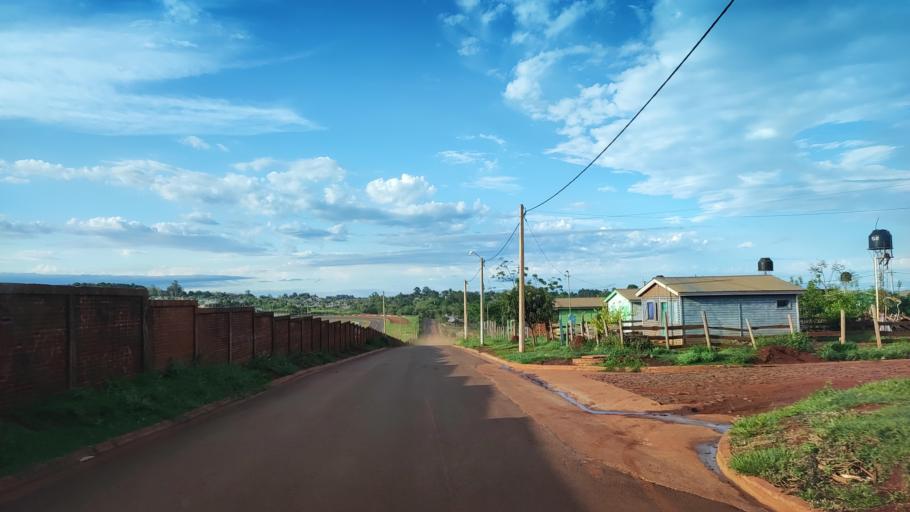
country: AR
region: Misiones
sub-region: Departamento de Capital
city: Posadas
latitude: -27.4411
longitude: -55.9245
